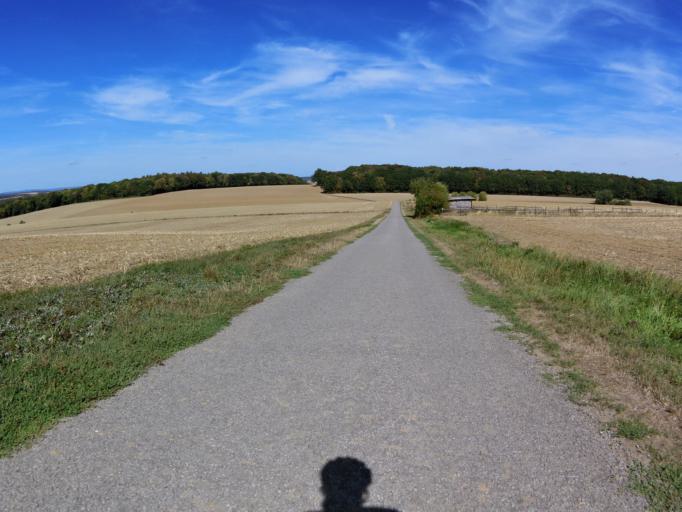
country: DE
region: Bavaria
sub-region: Regierungsbezirk Unterfranken
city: Eisingen
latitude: 49.7624
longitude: 9.8391
